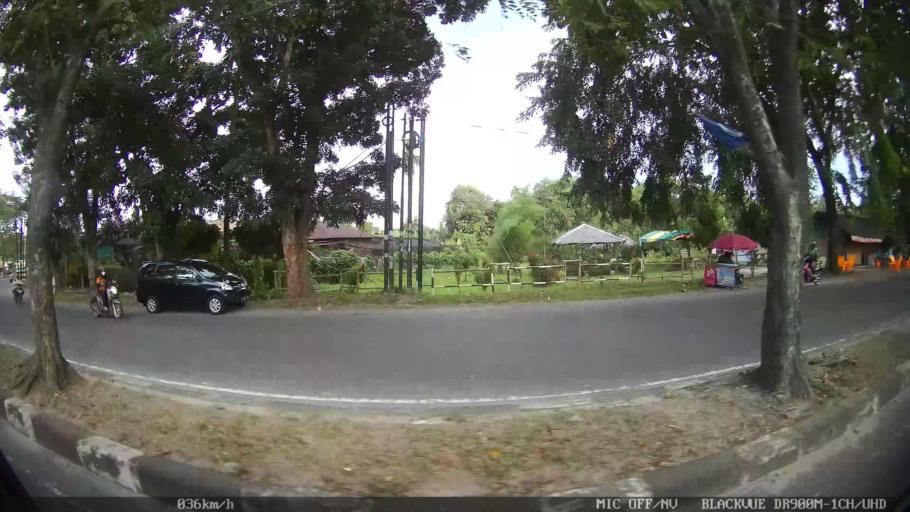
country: ID
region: North Sumatra
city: Sunggal
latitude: 3.5552
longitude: 98.6135
